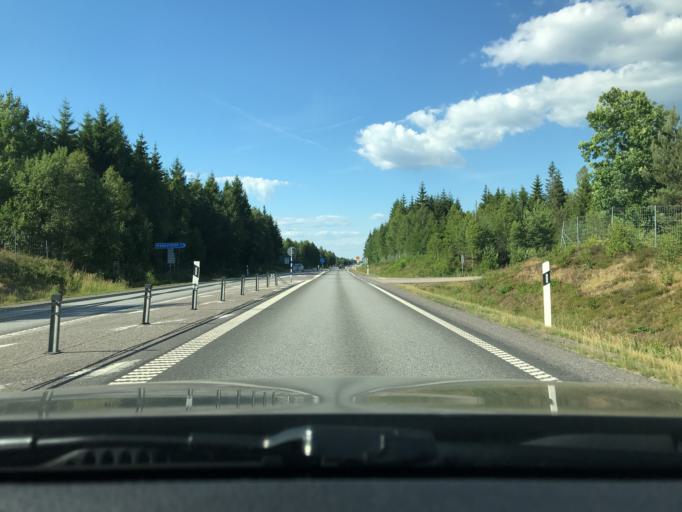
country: SE
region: Kronoberg
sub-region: Almhults Kommun
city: AElmhult
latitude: 56.4752
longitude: 14.1079
